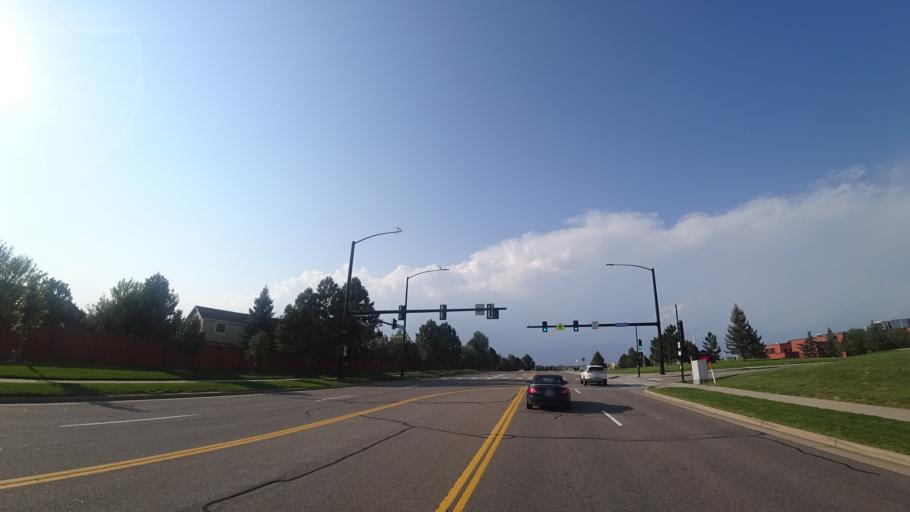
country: US
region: Colorado
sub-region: Arapahoe County
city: Dove Valley
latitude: 39.6199
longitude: -104.7387
